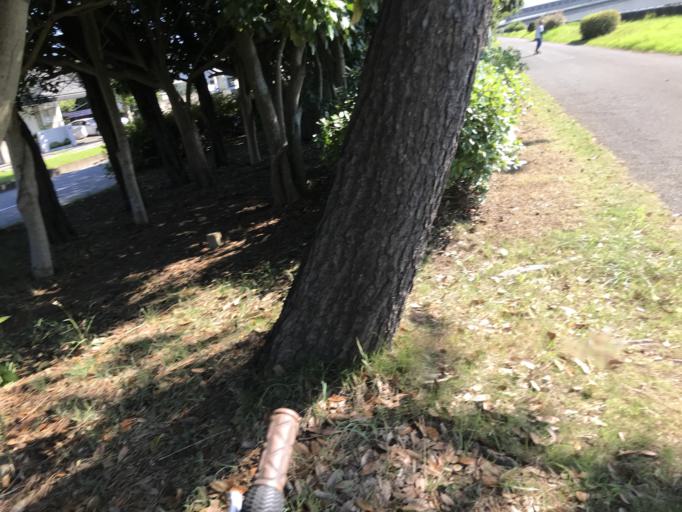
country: JP
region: Chiba
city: Chiba
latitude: 35.6431
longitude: 140.0562
